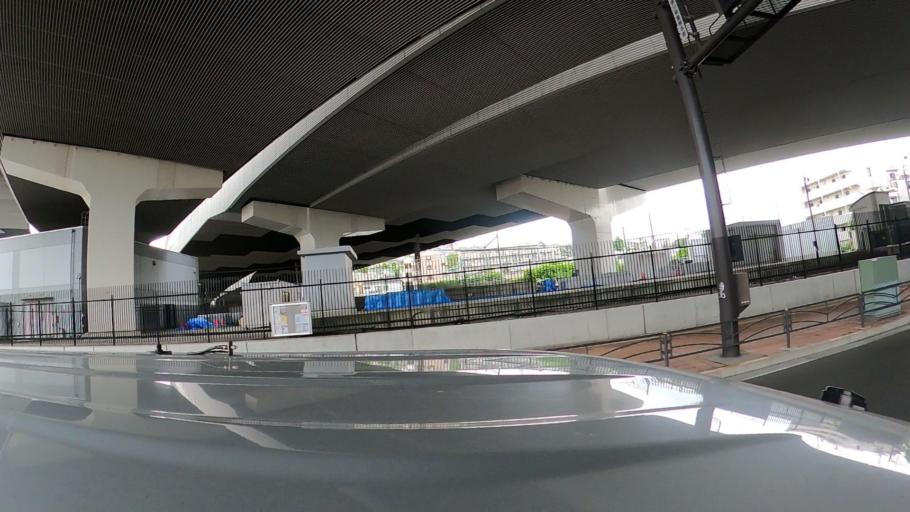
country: JP
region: Kanagawa
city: Yokohama
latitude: 35.4915
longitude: 139.6619
